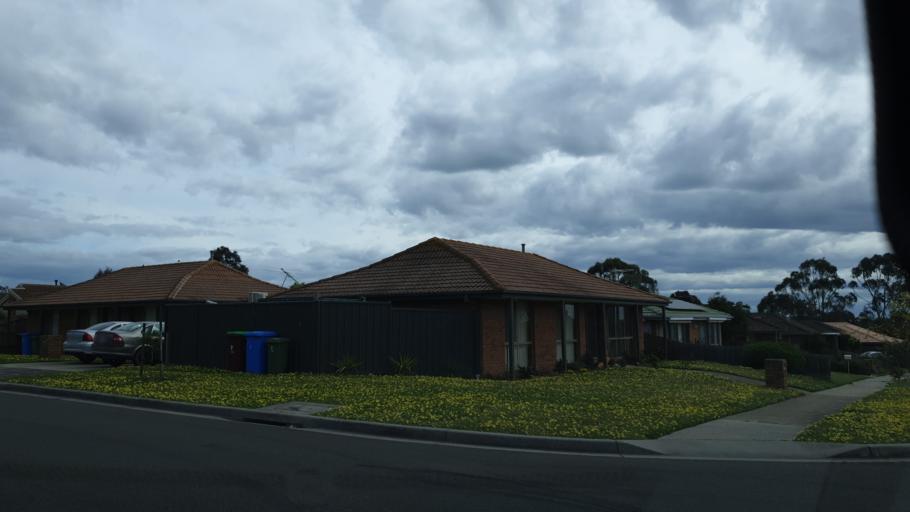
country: AU
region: Victoria
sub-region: Casey
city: Cranbourne North
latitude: -38.0770
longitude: 145.2802
